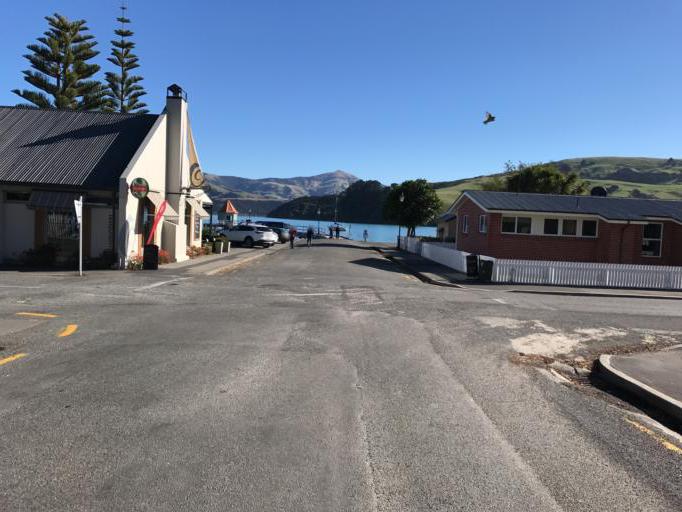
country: NZ
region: Canterbury
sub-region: Christchurch City
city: Christchurch
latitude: -43.8051
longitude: 172.9667
